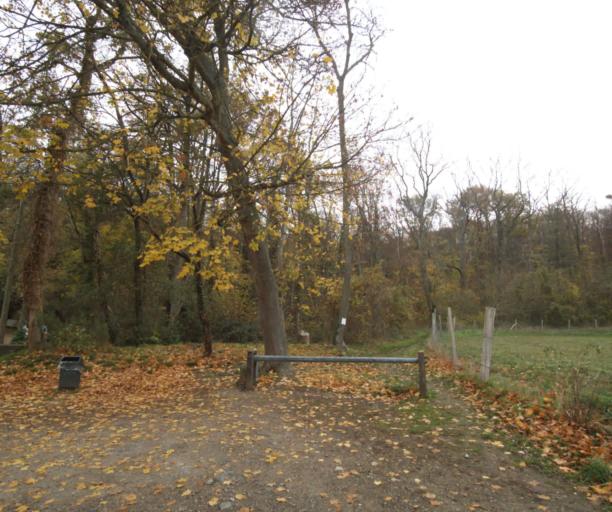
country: FR
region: Ile-de-France
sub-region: Departement des Yvelines
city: Triel-sur-Seine
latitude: 48.9870
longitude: 2.0107
